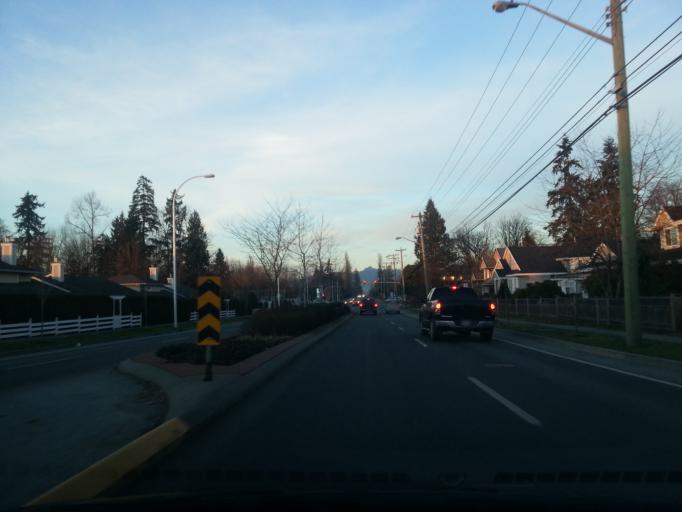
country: CA
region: British Columbia
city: Langley
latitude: 49.1270
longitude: -122.7125
